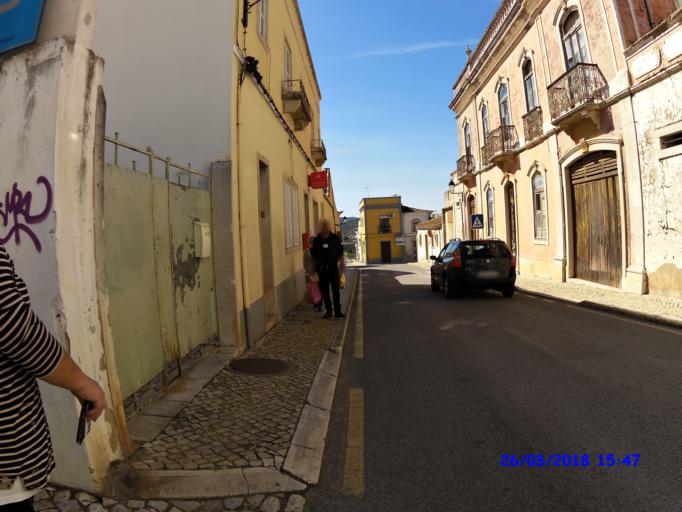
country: PT
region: Faro
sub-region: Loule
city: Boliqueime
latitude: 37.1761
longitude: -8.2003
